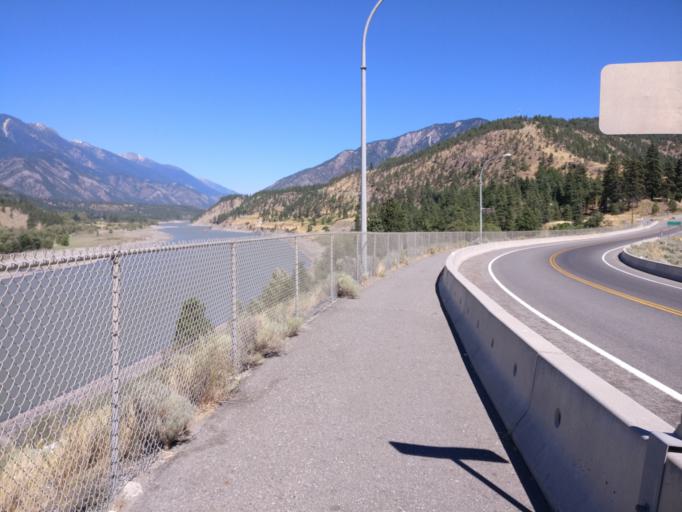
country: CA
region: British Columbia
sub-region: Thompson-Nicola Regional District
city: Ashcroft
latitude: 50.2370
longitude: -121.5820
